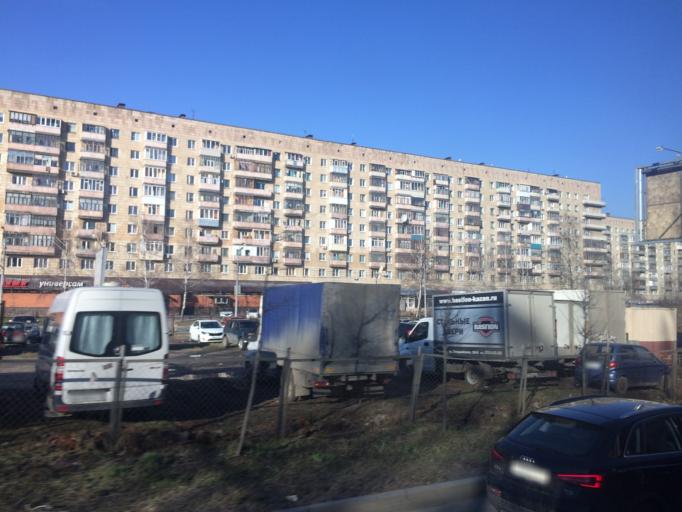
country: RU
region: Tatarstan
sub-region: Gorod Kazan'
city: Kazan
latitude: 55.8210
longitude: 49.0501
